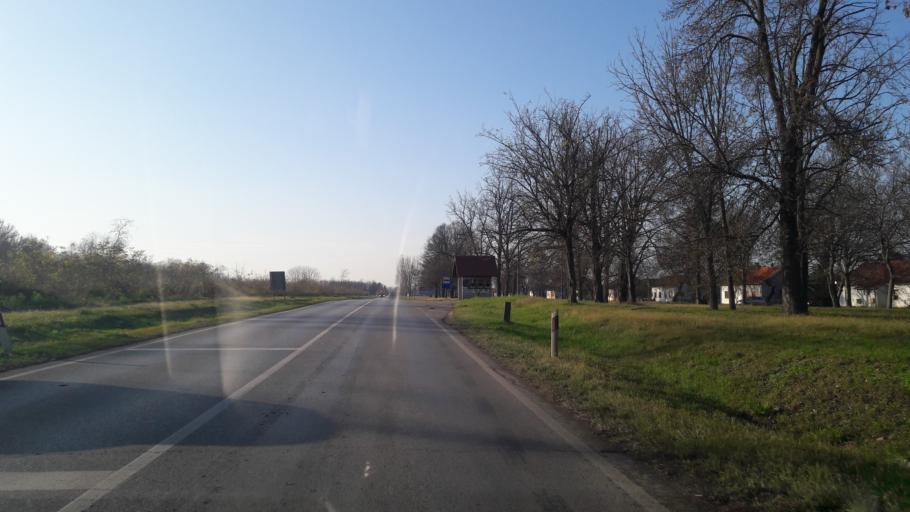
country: HR
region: Osjecko-Baranjska
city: Darda
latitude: 45.6210
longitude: 18.7183
